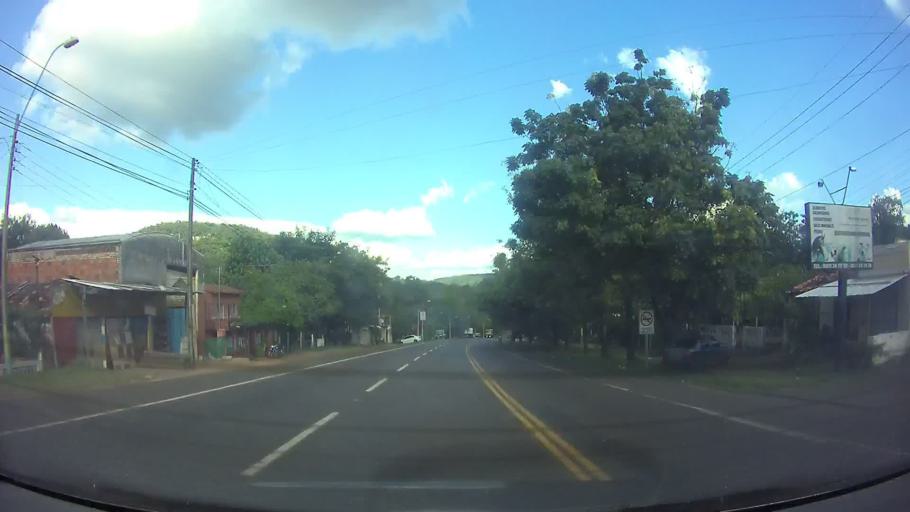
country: PY
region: Cordillera
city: Caacupe
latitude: -25.3841
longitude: -57.1271
